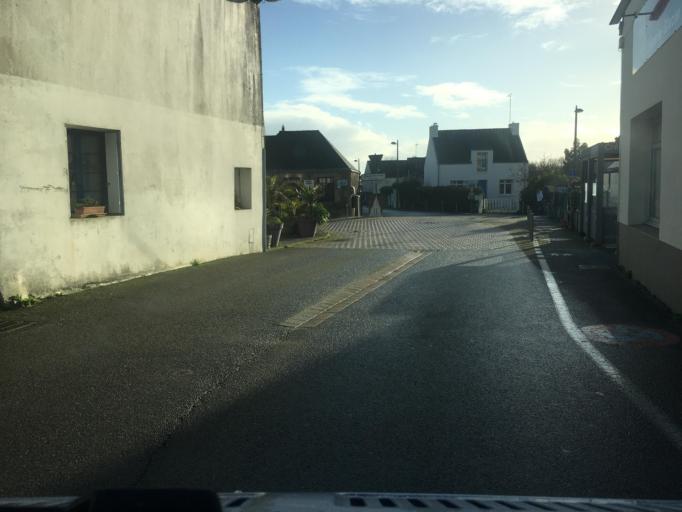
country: FR
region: Brittany
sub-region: Departement du Morbihan
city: Sarzeau
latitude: 47.5061
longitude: -2.6851
